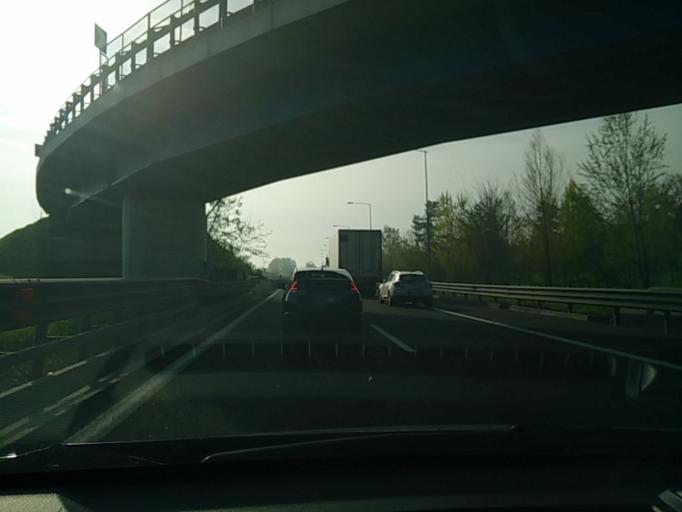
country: IT
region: Emilia-Romagna
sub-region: Provincia di Bologna
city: Bologna
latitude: 44.5186
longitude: 11.3719
